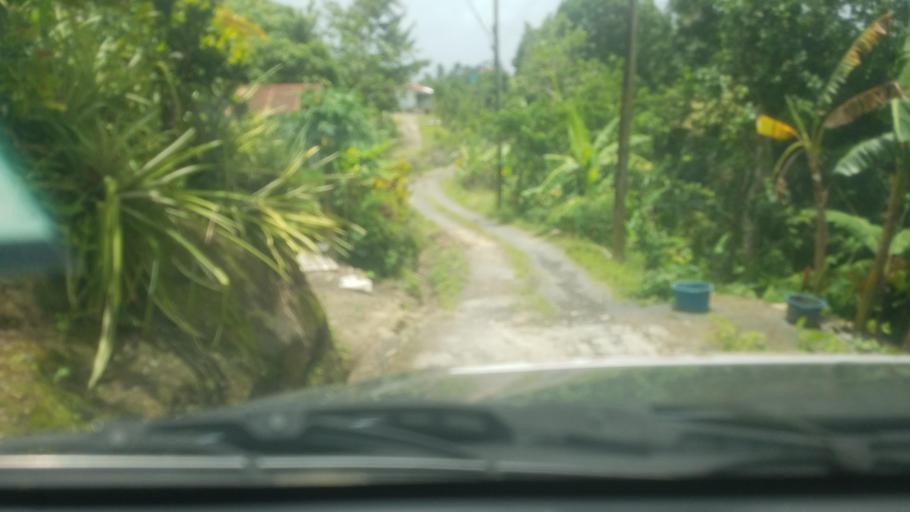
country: LC
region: Laborie Quarter
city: Laborie
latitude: 13.7830
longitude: -60.9939
